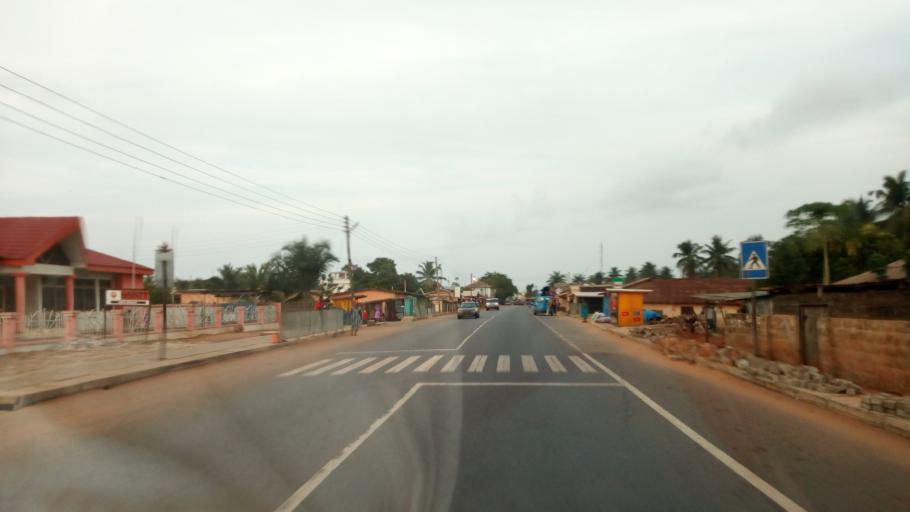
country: TG
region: Maritime
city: Lome
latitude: 6.1025
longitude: 1.1490
